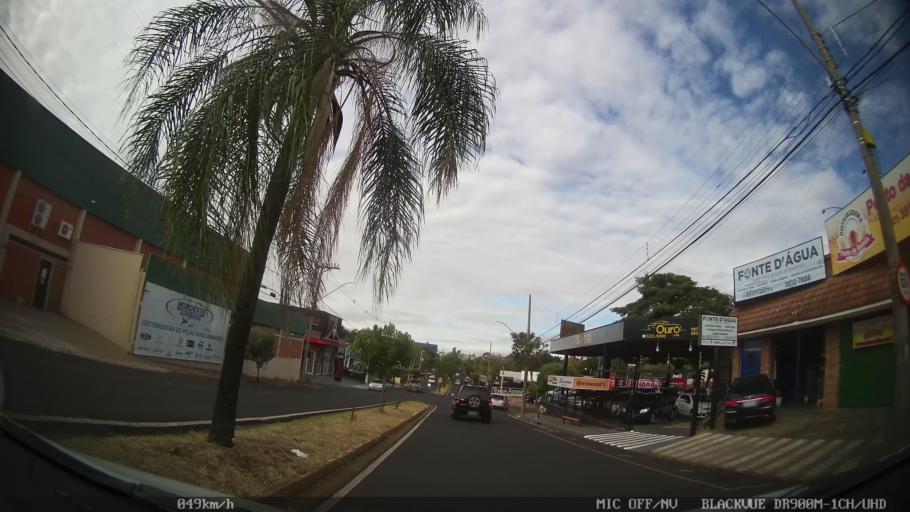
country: BR
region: Sao Paulo
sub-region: Sao Jose Do Rio Preto
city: Sao Jose do Rio Preto
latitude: -20.8360
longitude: -49.3712
